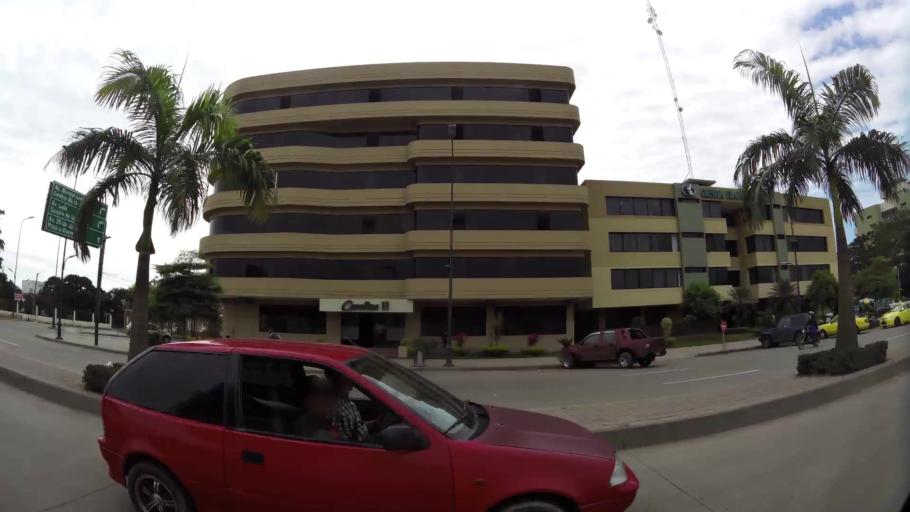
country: EC
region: El Oro
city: Machala
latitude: -3.2642
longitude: -79.9437
